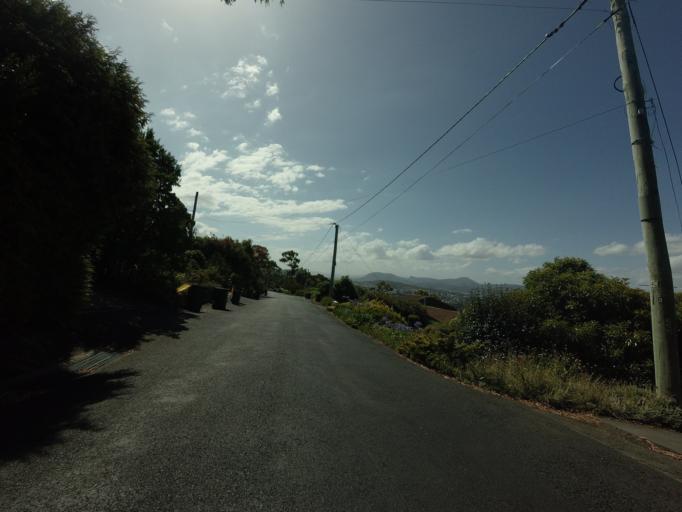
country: AU
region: Tasmania
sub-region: Hobart
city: Dynnyrne
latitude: -42.9113
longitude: 147.3264
